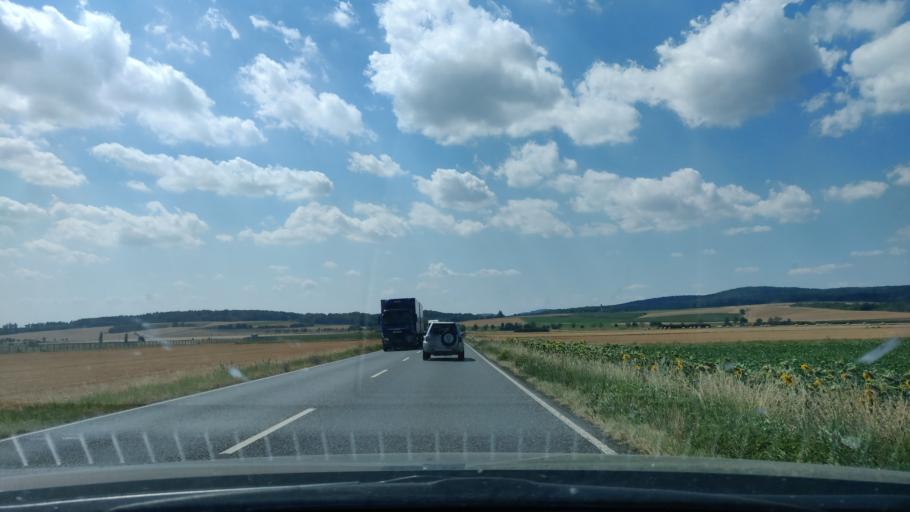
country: DE
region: Hesse
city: Fritzlar
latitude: 51.1167
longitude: 9.2755
